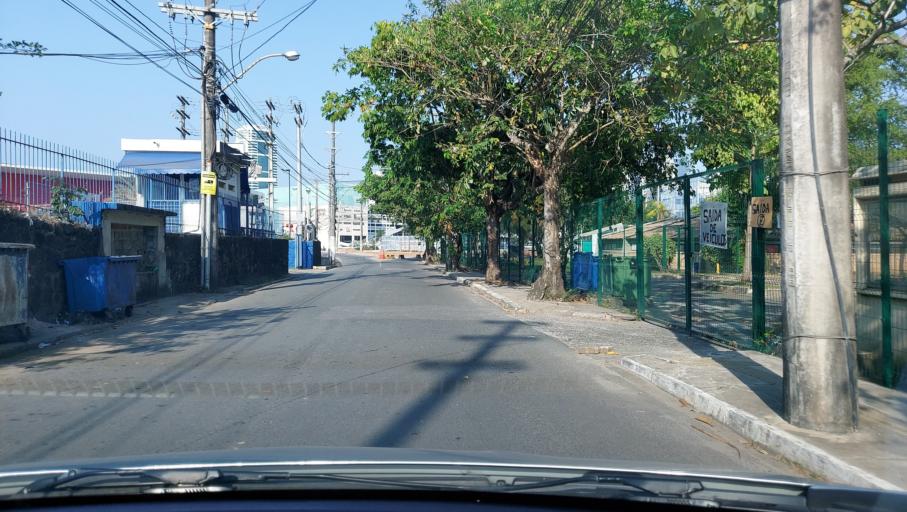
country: BR
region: Bahia
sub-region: Salvador
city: Salvador
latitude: -12.9832
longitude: -38.4679
